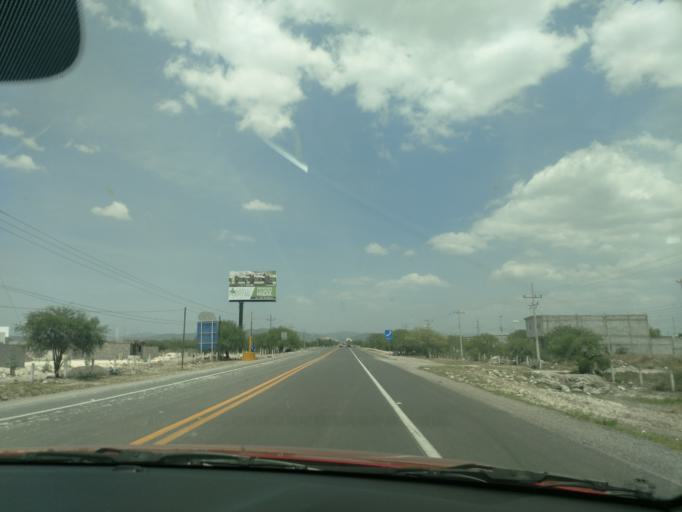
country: MX
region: San Luis Potosi
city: Rio Verde
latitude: 21.9179
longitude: -99.9498
